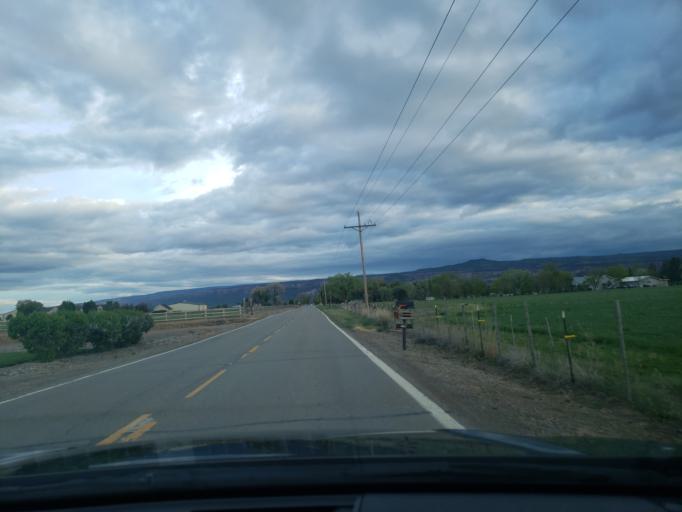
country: US
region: Colorado
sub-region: Mesa County
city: Fruita
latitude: 39.1758
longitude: -108.7013
